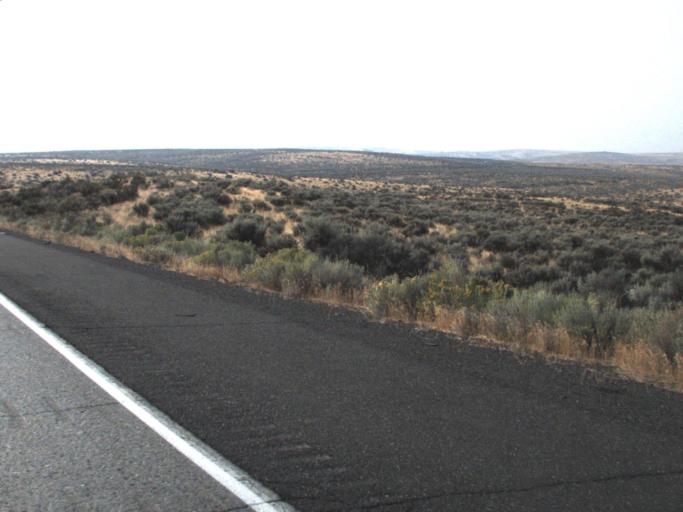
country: US
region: Washington
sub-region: Kittitas County
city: Kittitas
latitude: 46.8292
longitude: -120.3668
